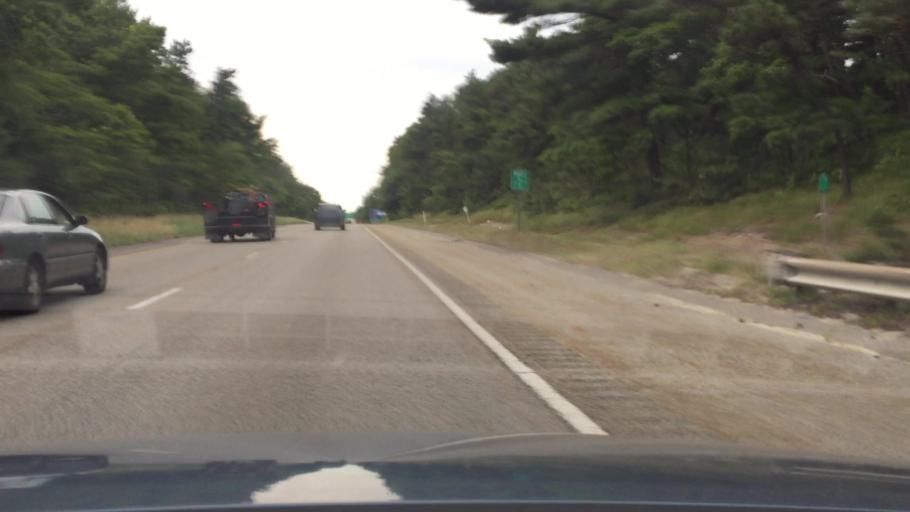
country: US
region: Massachusetts
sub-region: Plymouth County
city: White Island Shores
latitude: 41.8609
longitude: -70.5873
